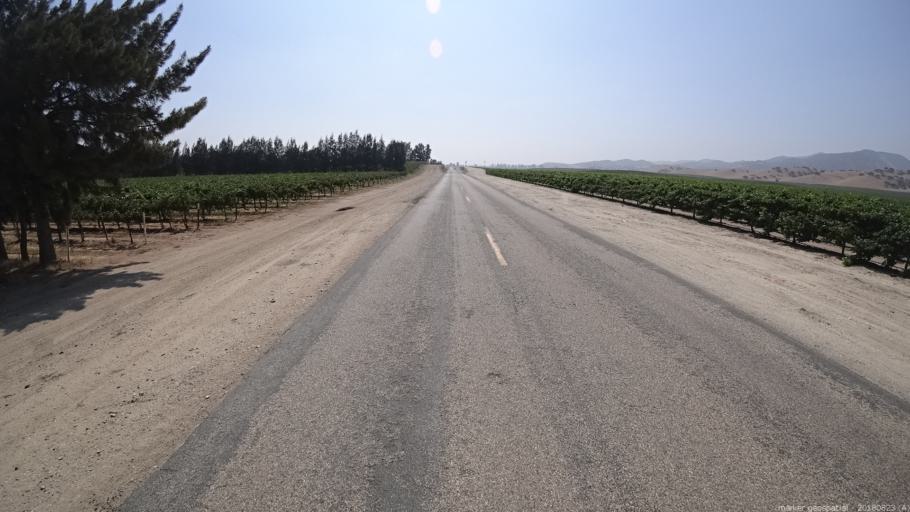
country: US
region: California
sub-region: Monterey County
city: King City
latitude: 36.2462
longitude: -121.1913
